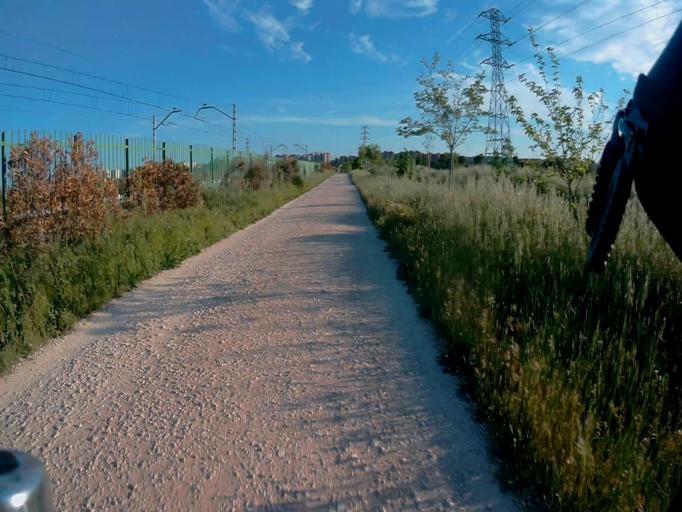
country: ES
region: Madrid
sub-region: Provincia de Madrid
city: Fuenlabrada
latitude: 40.3040
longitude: -3.7884
